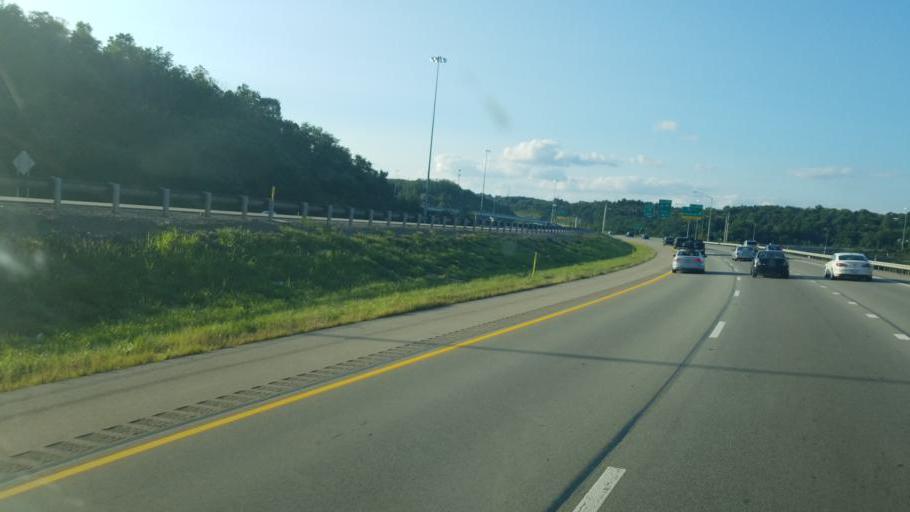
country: US
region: Pennsylvania
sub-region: Allegheny County
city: Carnegie
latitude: 40.4175
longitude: -80.1029
